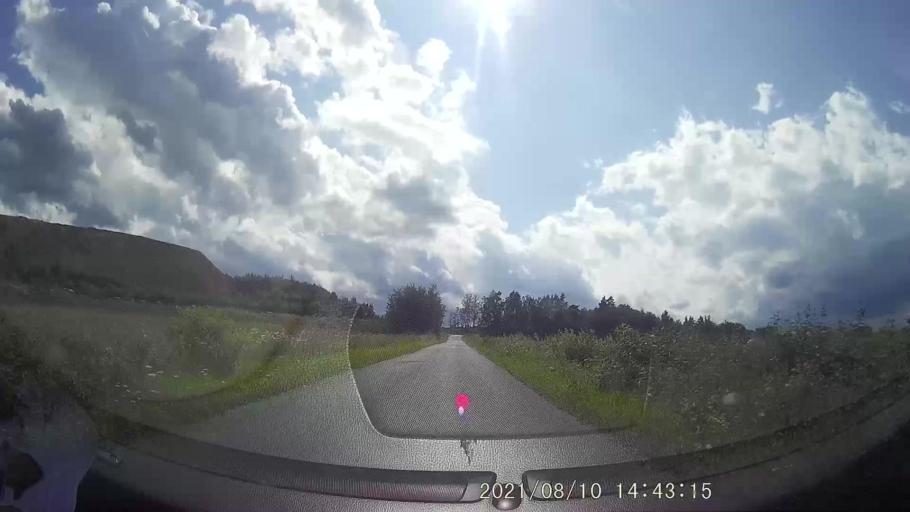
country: PL
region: Lower Silesian Voivodeship
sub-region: Powiat klodzki
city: Radkow
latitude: 50.5481
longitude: 16.4300
